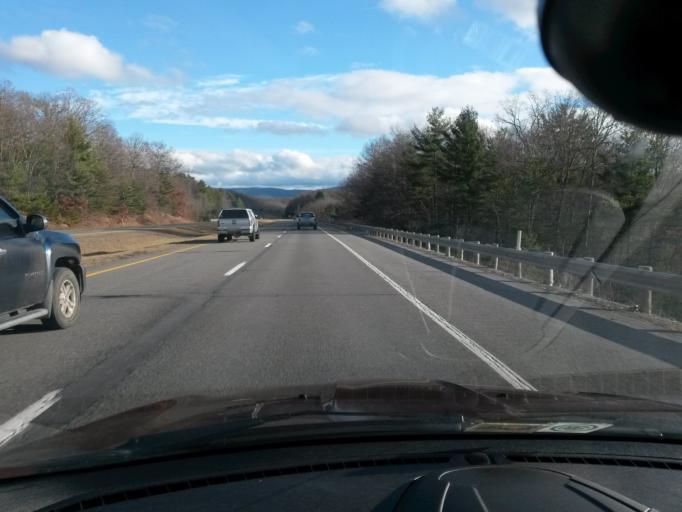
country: US
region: West Virginia
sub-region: Mercer County
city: Athens
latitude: 37.3581
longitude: -81.0250
